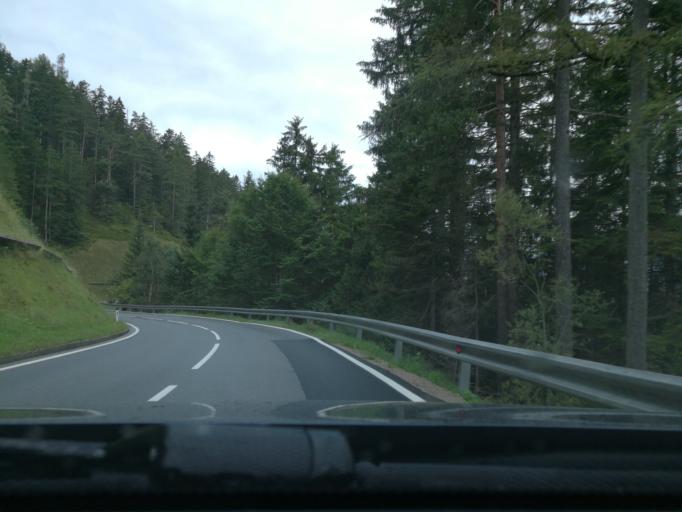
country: AT
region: Salzburg
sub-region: Politischer Bezirk Sankt Johann im Pongau
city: Radstadt
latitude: 47.3821
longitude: 13.4924
